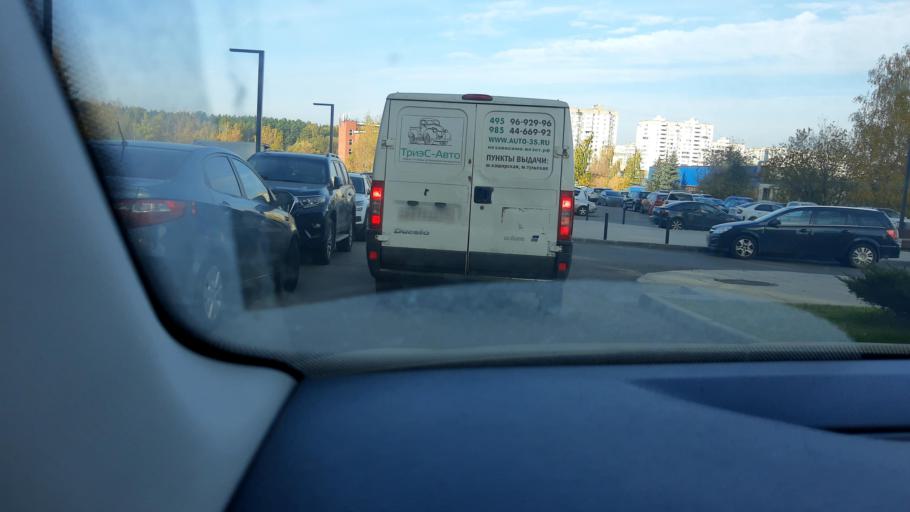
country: RU
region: Moscow
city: Annino
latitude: 55.5604
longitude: 37.5765
